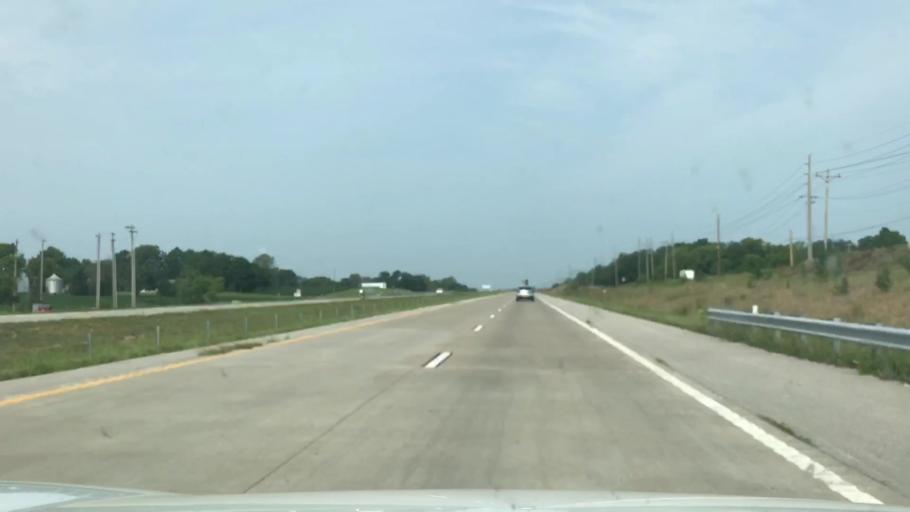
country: US
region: Missouri
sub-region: Saint Charles County
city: Dardenne Prairie
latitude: 38.7612
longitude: -90.7194
